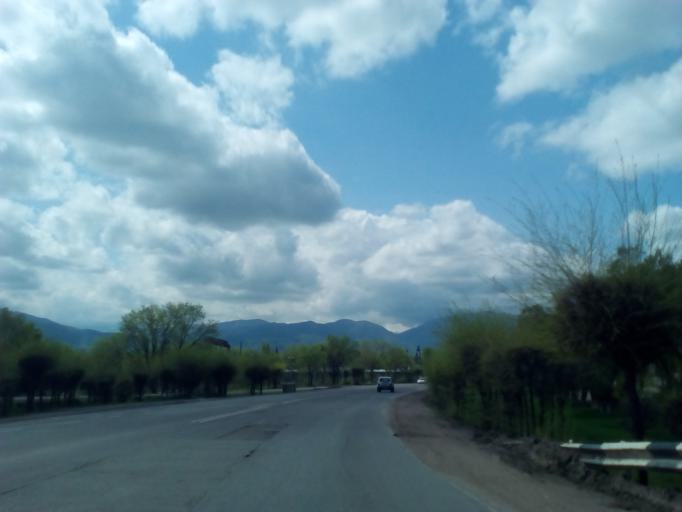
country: KZ
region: Almaty Oblysy
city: Burunday
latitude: 43.2170
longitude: 76.6473
